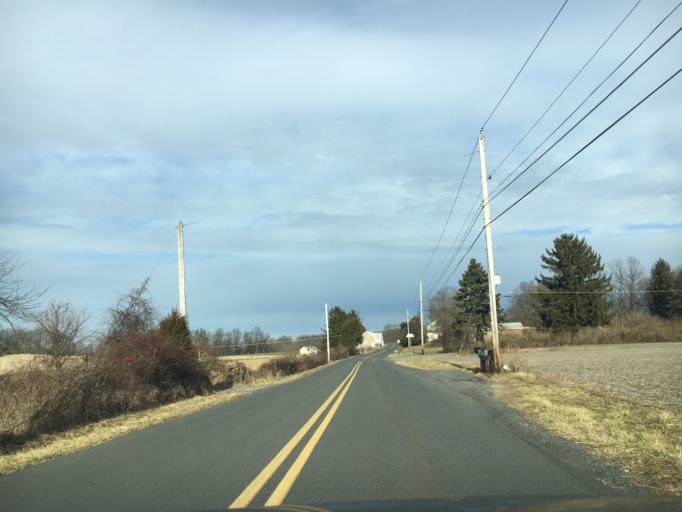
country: US
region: Pennsylvania
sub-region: Berks County
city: Stony Creek Mills
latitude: 40.3812
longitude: -75.8404
